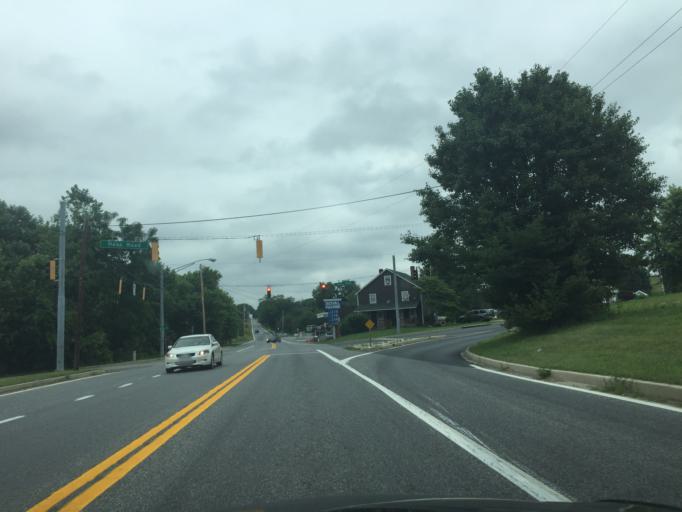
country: US
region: Maryland
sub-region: Harford County
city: Jarrettsville
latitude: 39.5541
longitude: -76.5258
